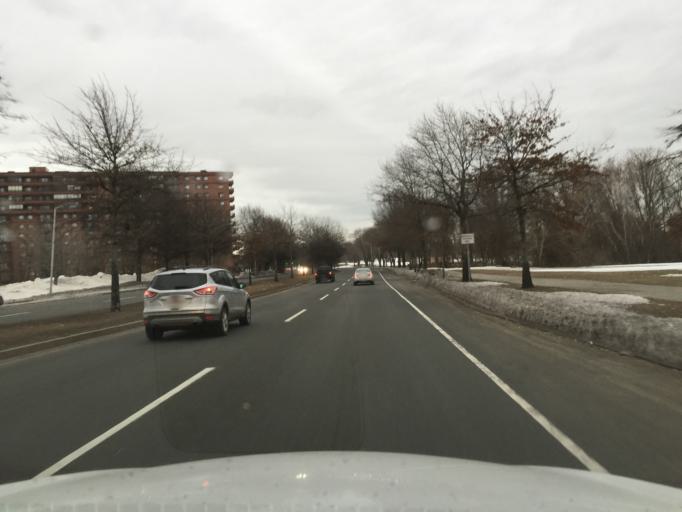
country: US
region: Massachusetts
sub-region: Middlesex County
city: Medford
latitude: 42.4054
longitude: -71.0936
